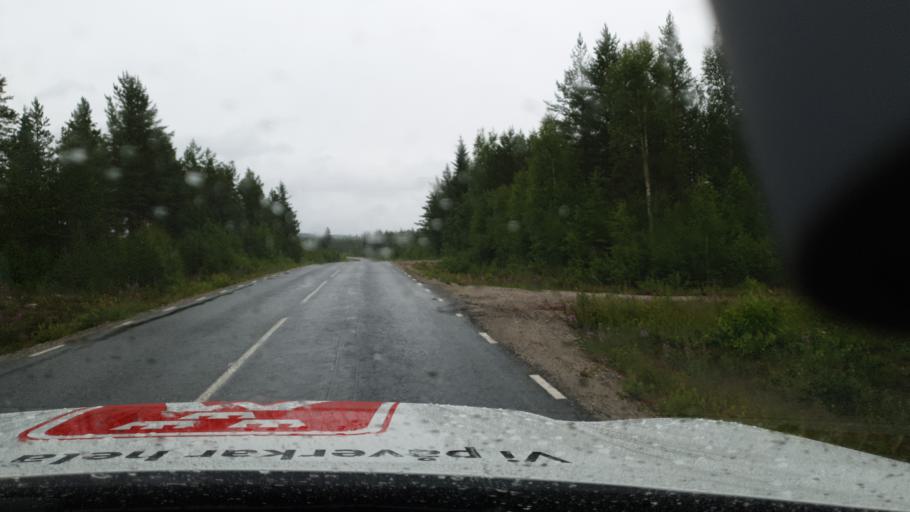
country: SE
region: Vaesterbotten
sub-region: Vindelns Kommun
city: Vindeln
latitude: 64.4215
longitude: 19.6971
